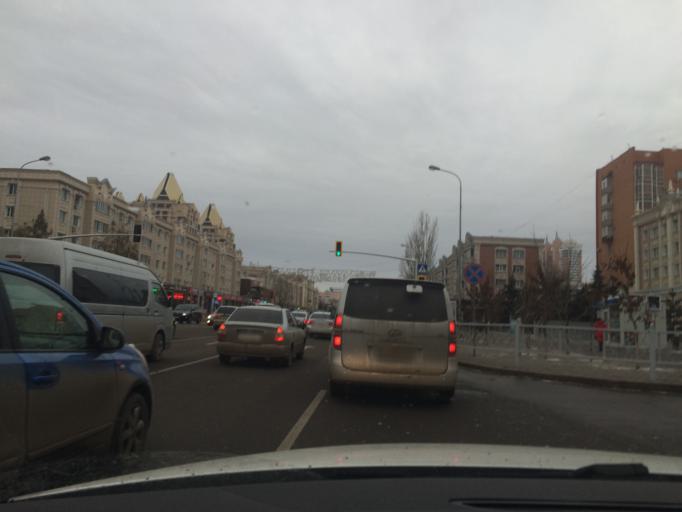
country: KZ
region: Astana Qalasy
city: Astana
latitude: 51.1581
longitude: 71.4296
